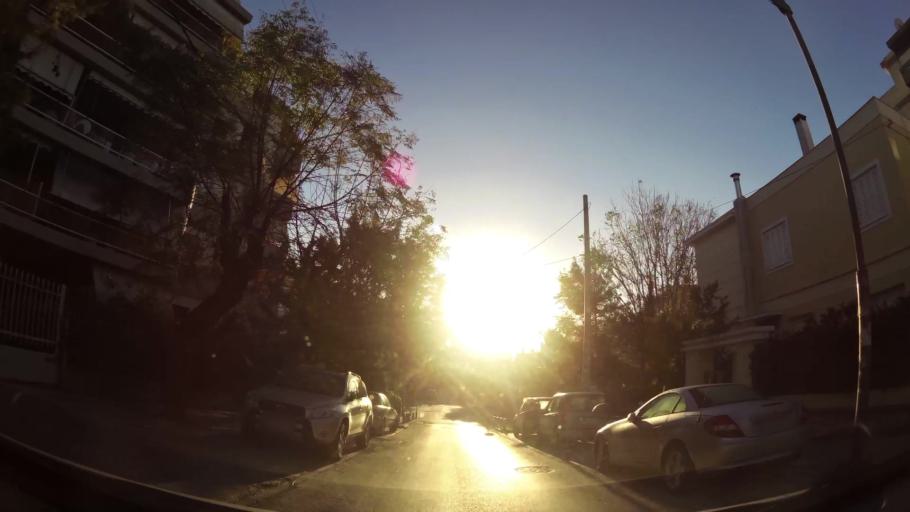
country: GR
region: Attica
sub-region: Nomarchia Athinas
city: Marousi
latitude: 38.0557
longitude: 23.8004
